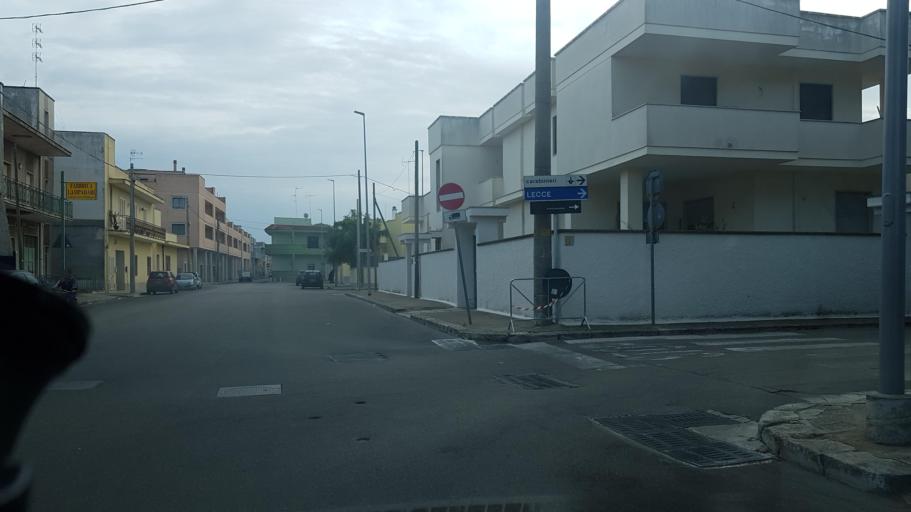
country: IT
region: Apulia
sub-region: Provincia di Lecce
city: Trepuzzi
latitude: 40.4103
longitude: 18.0704
